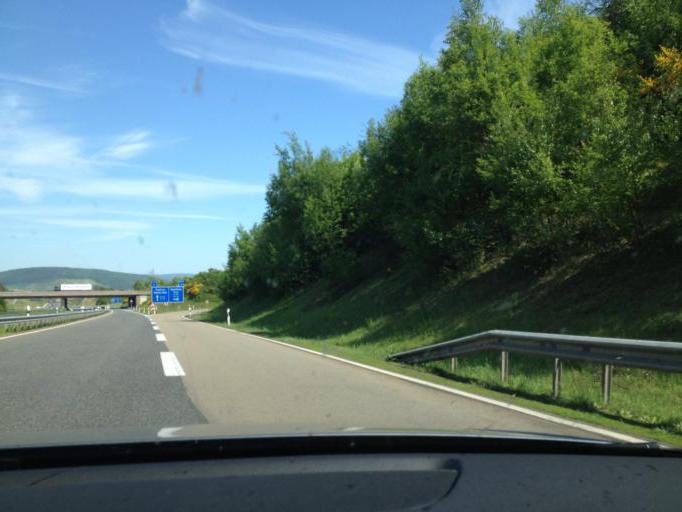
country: DE
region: Rheinland-Pfalz
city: Salmtal
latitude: 49.9480
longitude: 6.8783
